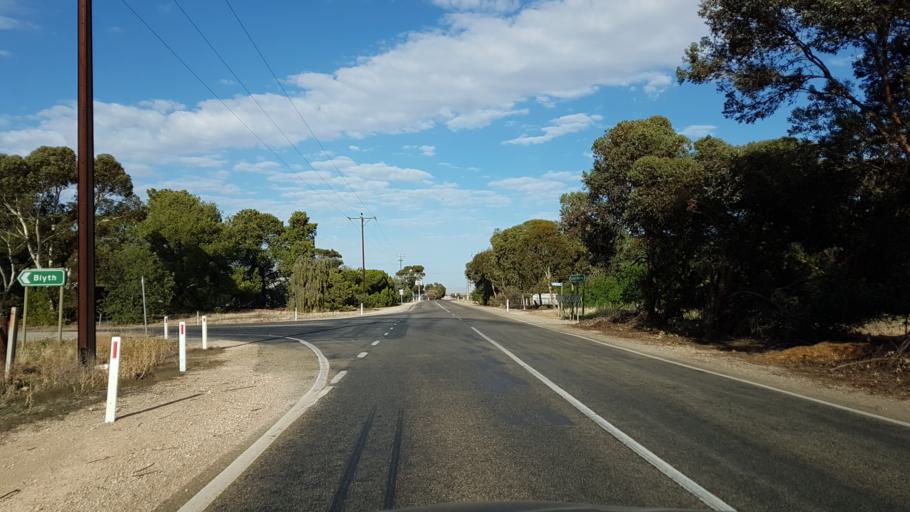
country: AU
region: South Australia
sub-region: Clare and Gilbert Valleys
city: Clare
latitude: -33.7038
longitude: 138.4052
